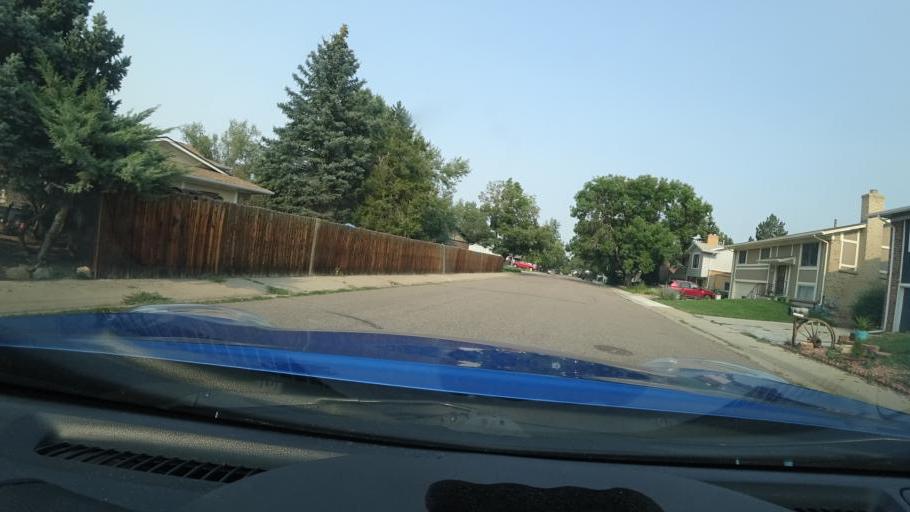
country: US
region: Colorado
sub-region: Adams County
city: Aurora
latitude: 39.6680
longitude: -104.7850
